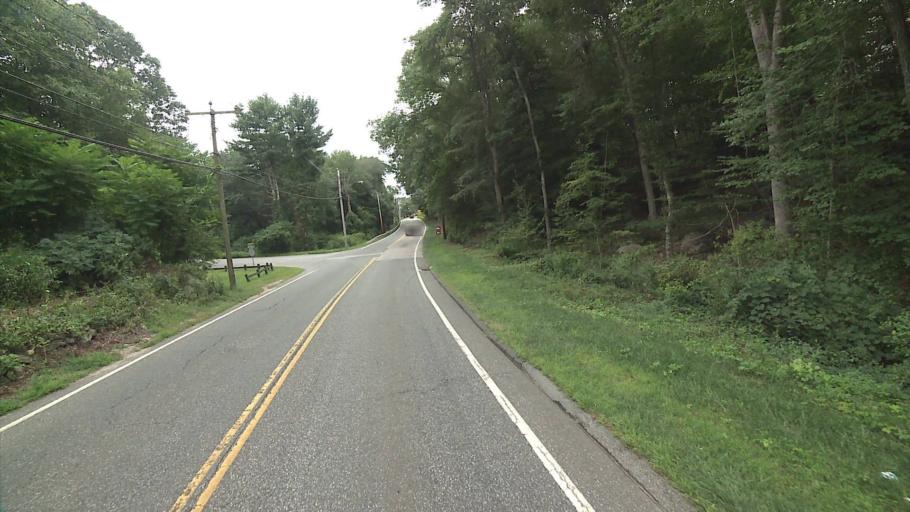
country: US
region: Connecticut
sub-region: New London County
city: Niantic
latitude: 41.3006
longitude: -72.2576
